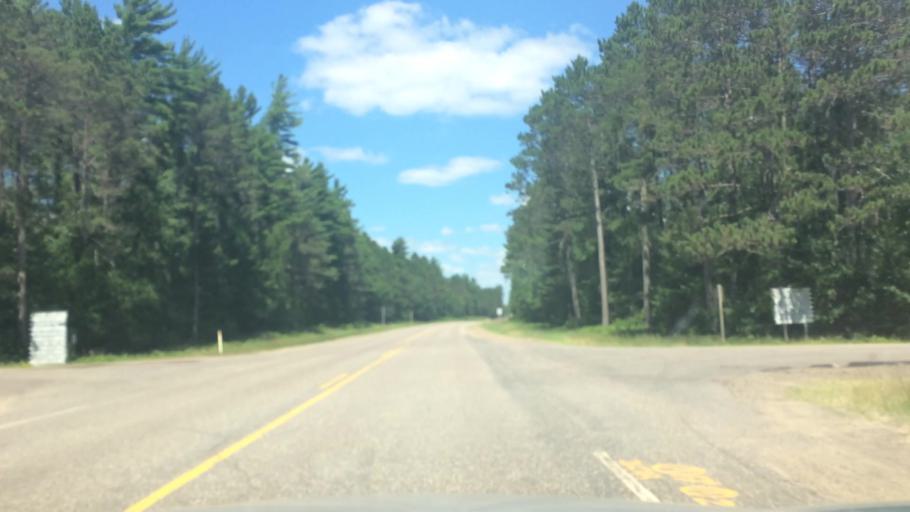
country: US
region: Wisconsin
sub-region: Vilas County
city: Lac du Flambeau
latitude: 46.0834
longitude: -89.6451
